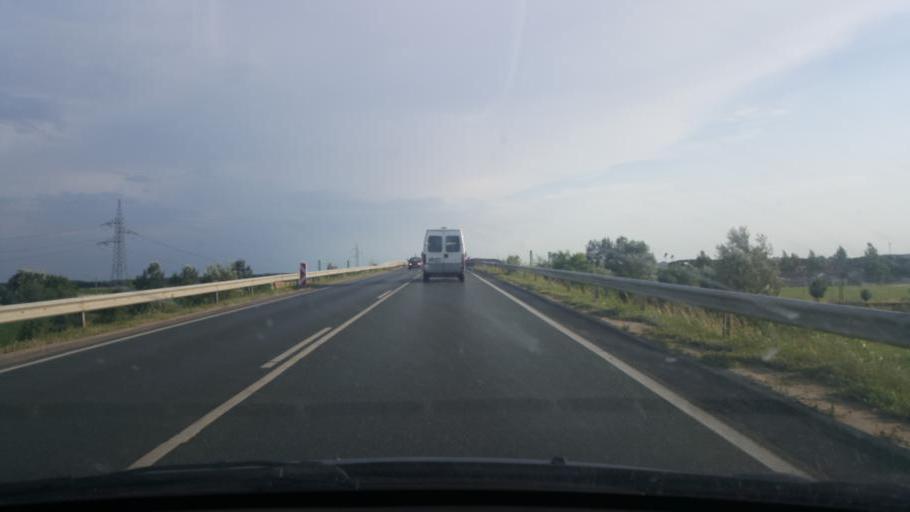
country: HU
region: Pest
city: Ullo
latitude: 47.3868
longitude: 19.3666
